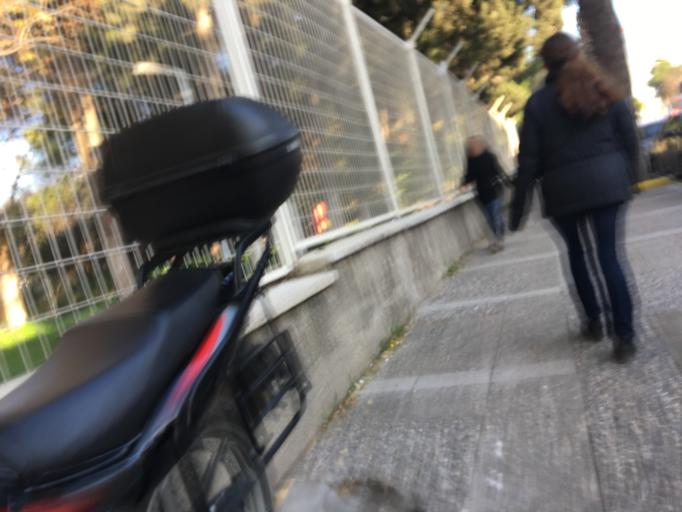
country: TR
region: Izmir
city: Buca
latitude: 38.3891
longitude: 27.1704
